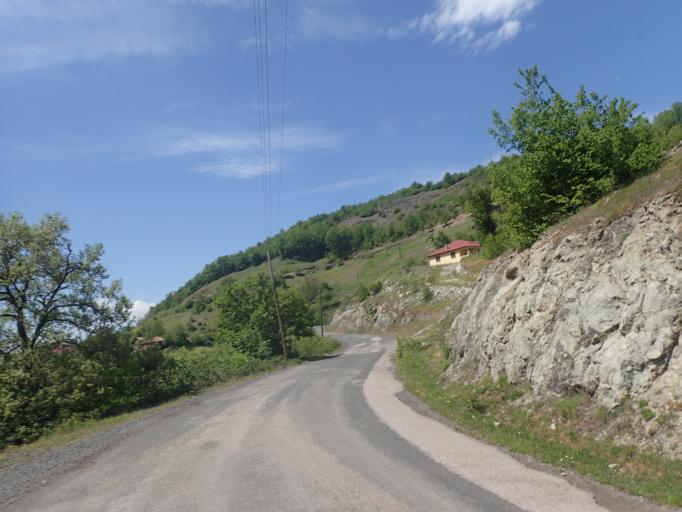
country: TR
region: Ordu
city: Akkus
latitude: 40.8005
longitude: 36.9417
